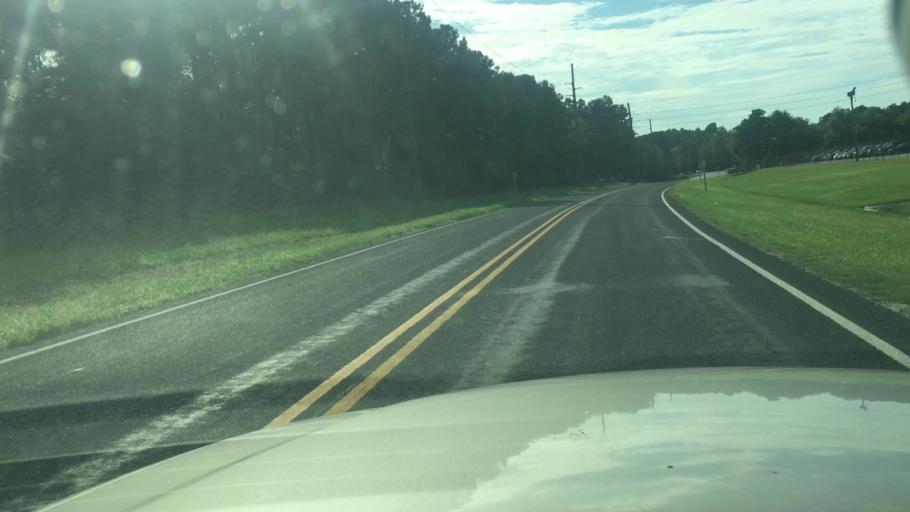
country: US
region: North Carolina
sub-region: Cumberland County
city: Eastover
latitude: 35.1656
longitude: -78.8583
